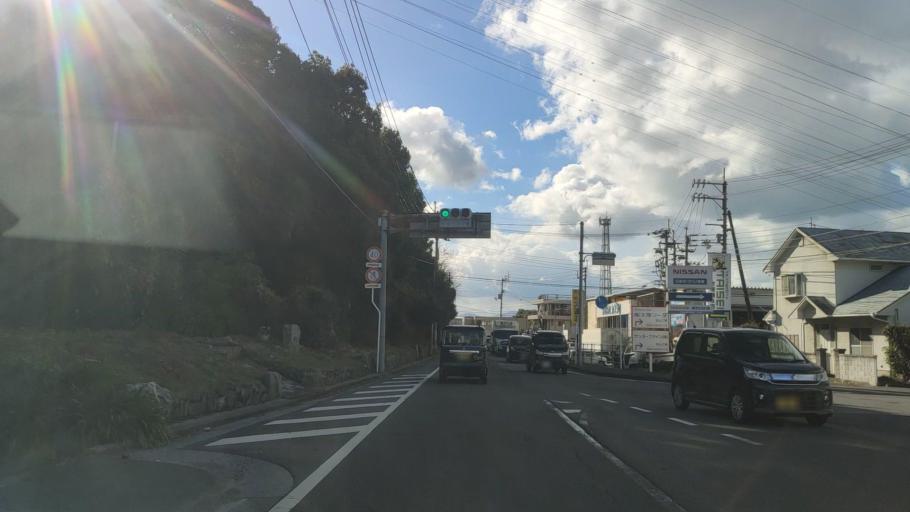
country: JP
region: Ehime
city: Masaki-cho
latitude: 33.8436
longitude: 132.7081
